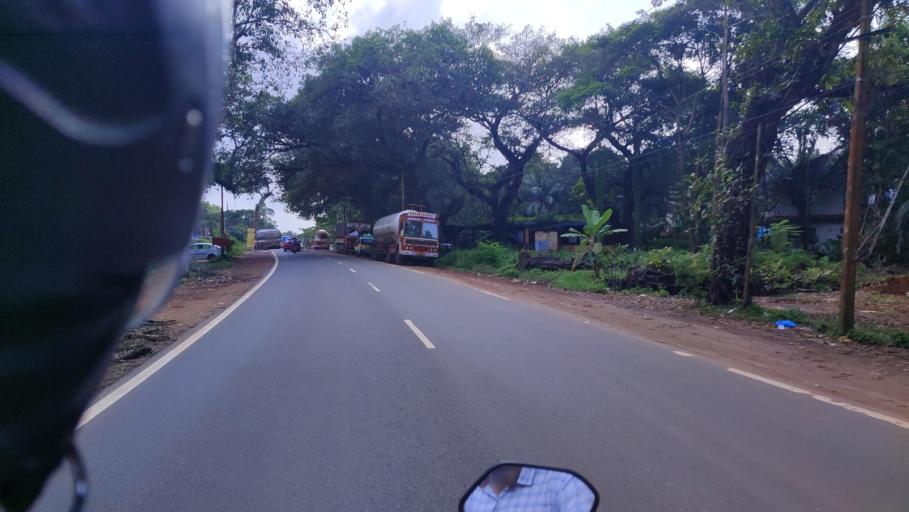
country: IN
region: Kerala
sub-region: Kasaragod District
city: Nileshwar
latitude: 12.2273
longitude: 75.1568
